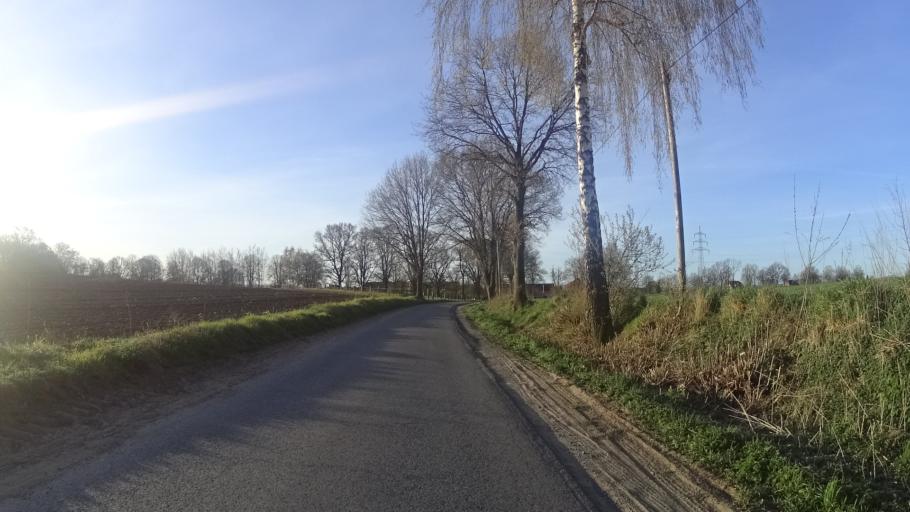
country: DE
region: North Rhine-Westphalia
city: Emsdetten
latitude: 52.2031
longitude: 7.5255
